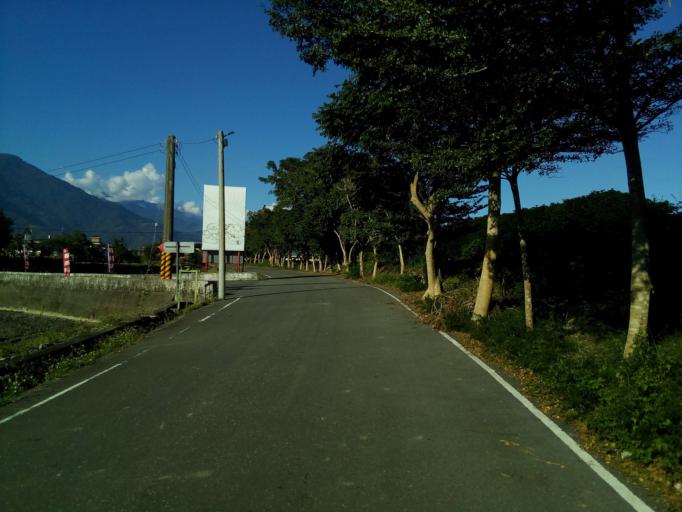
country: TW
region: Taiwan
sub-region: Taitung
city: Taitung
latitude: 23.0392
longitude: 121.1711
